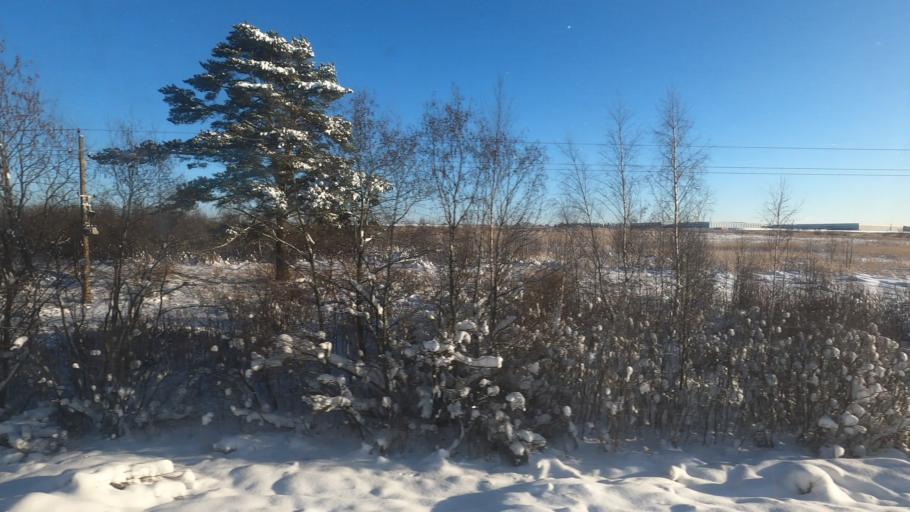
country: RU
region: Moskovskaya
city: Orud'yevo
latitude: 56.4272
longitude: 37.4986
